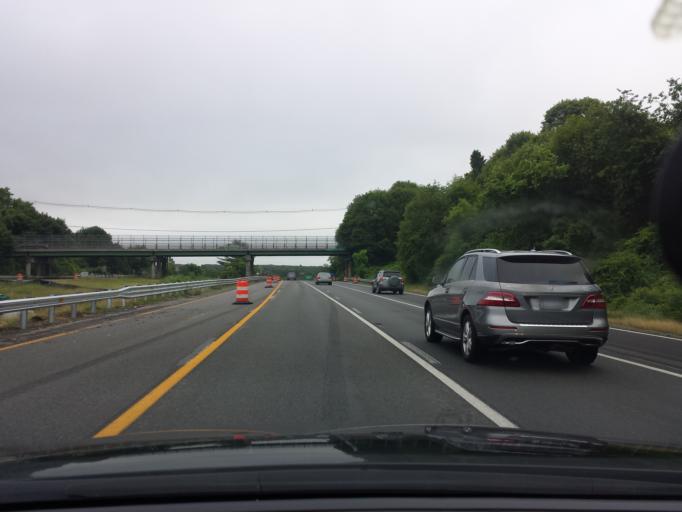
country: US
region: Massachusetts
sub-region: Bristol County
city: Ocean Grove
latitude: 41.7335
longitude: -71.1985
